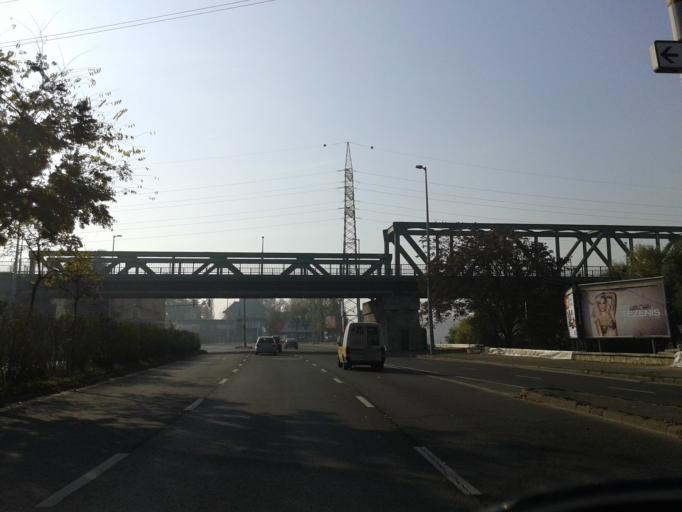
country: HU
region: Budapest
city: Budapest IV. keruelet
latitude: 47.5610
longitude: 19.0777
